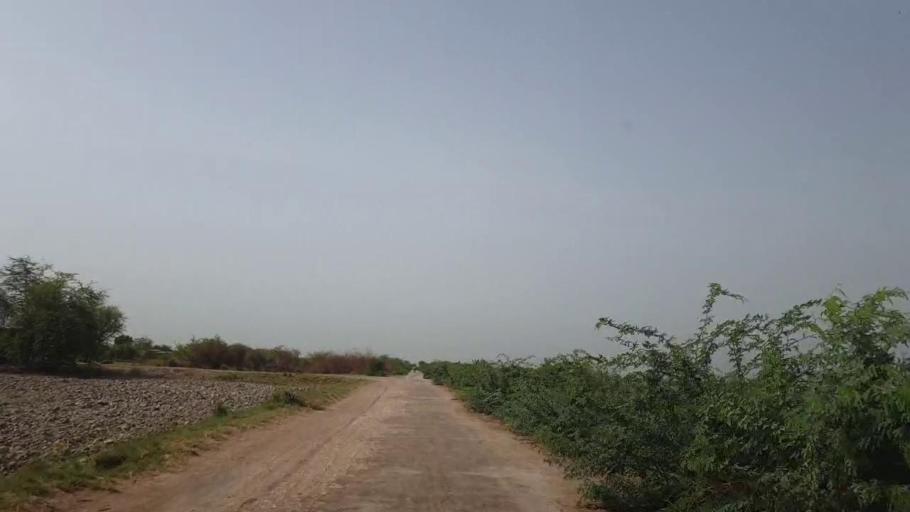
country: PK
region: Sindh
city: Nawabshah
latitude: 26.1142
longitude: 68.4397
